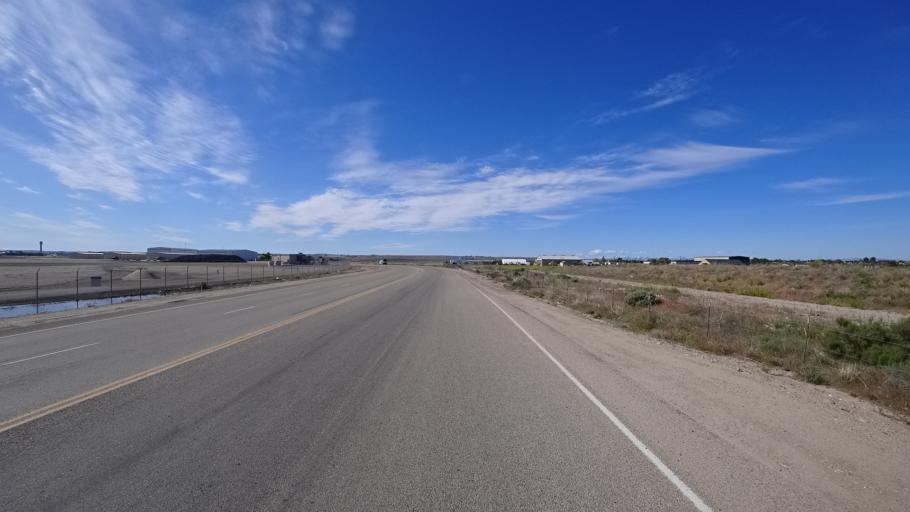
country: US
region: Idaho
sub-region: Ada County
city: Garden City
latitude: 43.5711
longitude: -116.2490
